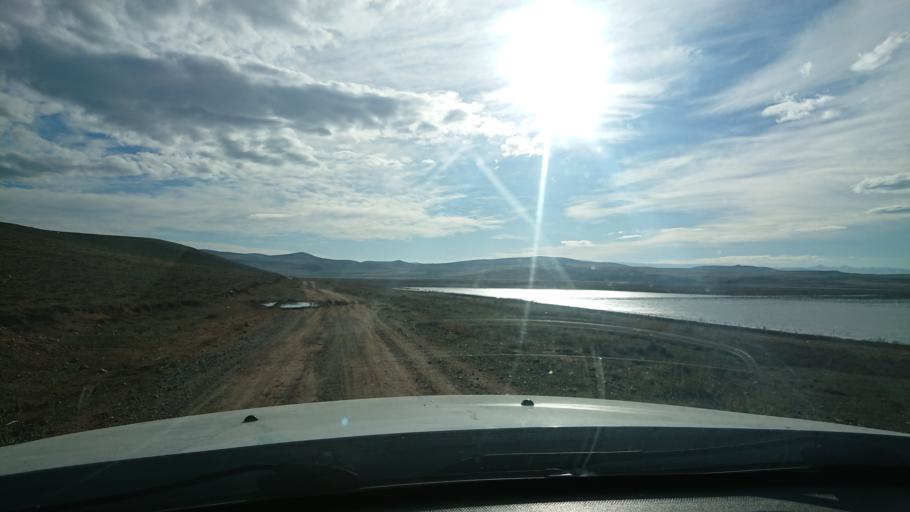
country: TR
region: Aksaray
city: Sariyahsi
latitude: 39.0456
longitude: 33.9720
